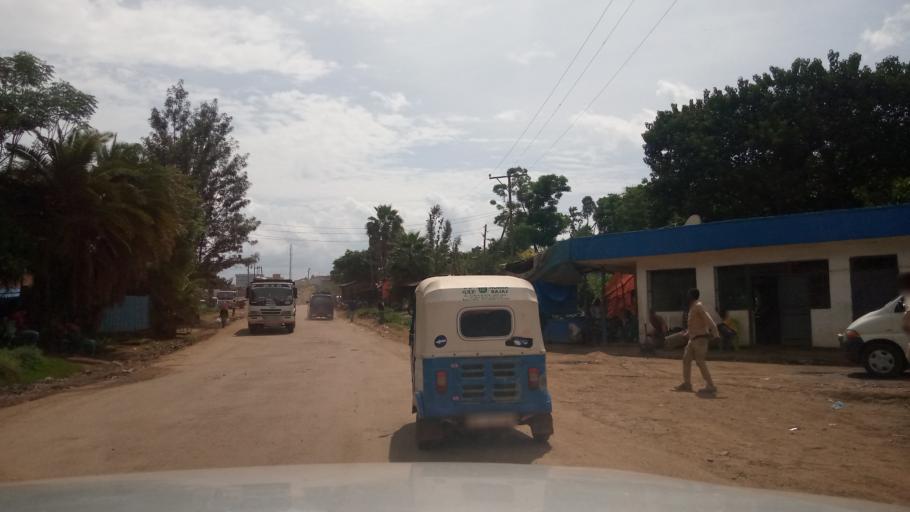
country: ET
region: Oromiya
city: Agaro
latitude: 7.8544
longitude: 36.5920
